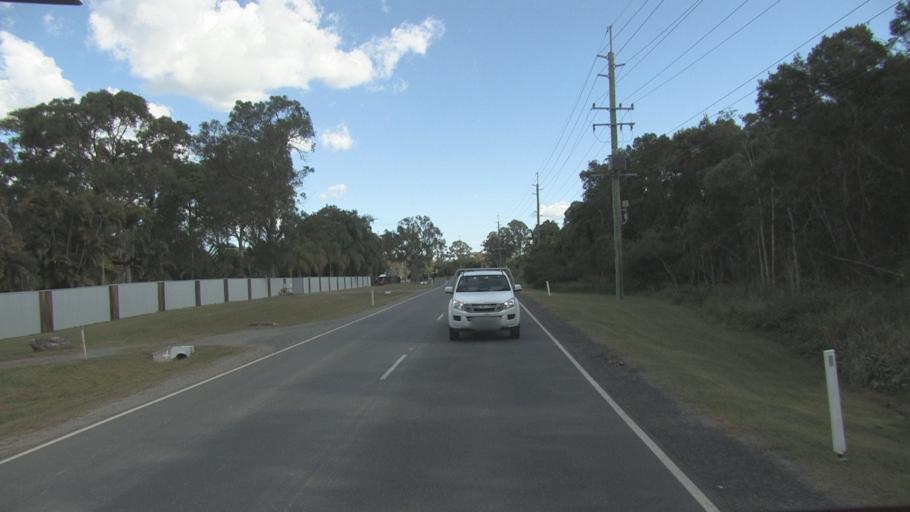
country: AU
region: Queensland
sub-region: Logan
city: Beenleigh
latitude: -27.6599
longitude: 153.2185
